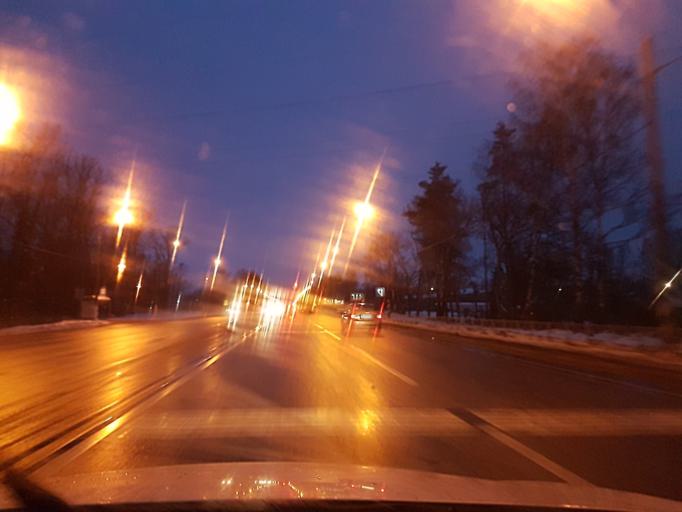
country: RU
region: Tverskaya
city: Zavidovo
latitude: 56.5770
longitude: 36.4970
